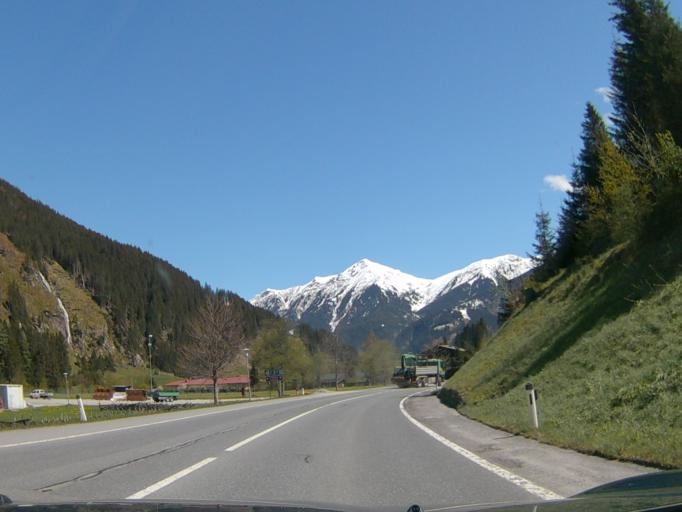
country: AT
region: Salzburg
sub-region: Politischer Bezirk Sankt Johann im Pongau
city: Bad Gastein
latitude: 47.0959
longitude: 13.1242
